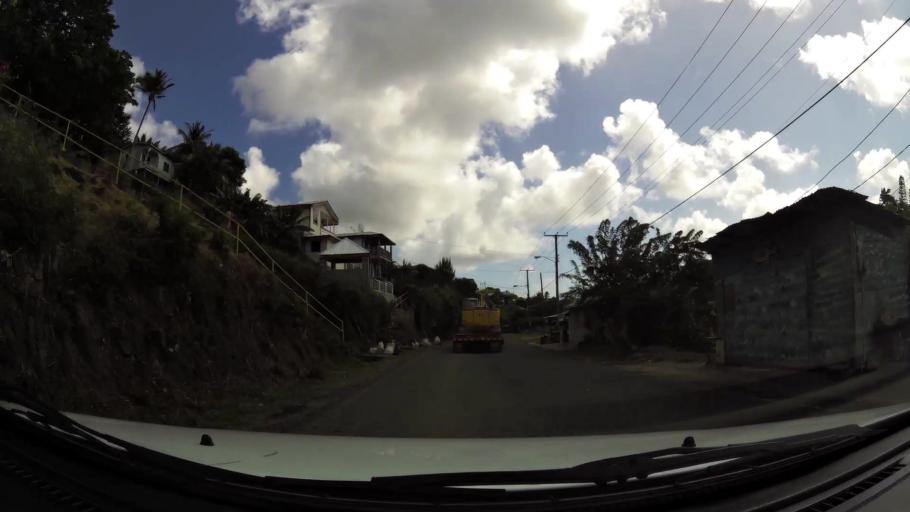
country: LC
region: Laborie Quarter
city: Laborie
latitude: 13.7538
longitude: -60.9976
